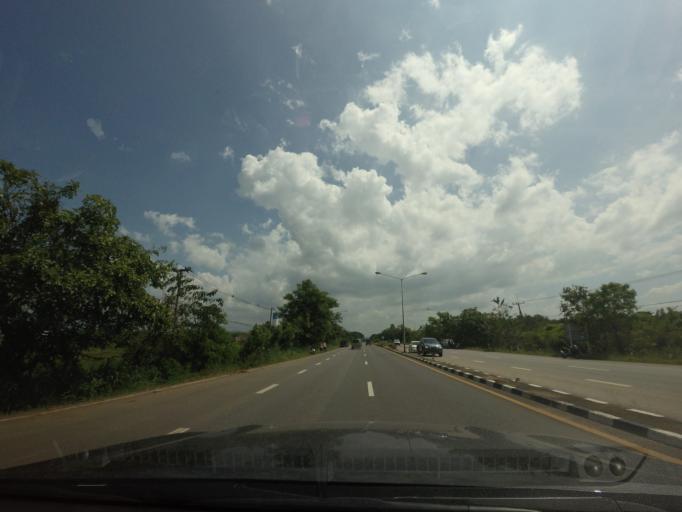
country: TH
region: Phetchabun
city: Phetchabun
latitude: 16.2354
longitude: 101.0811
